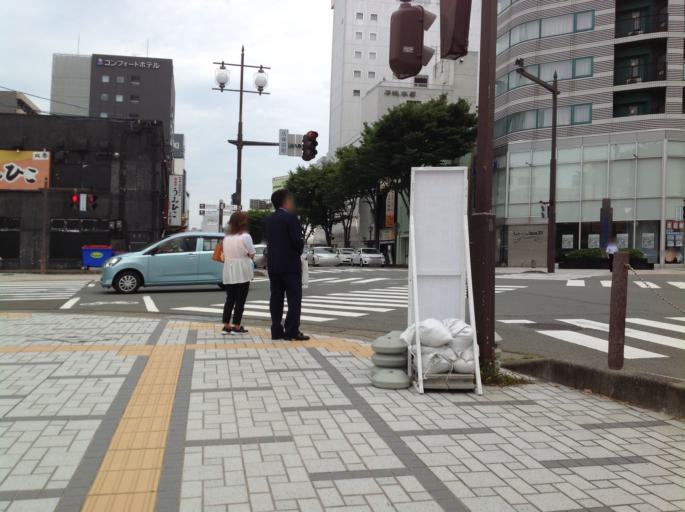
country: JP
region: Akita
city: Akita
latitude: 39.7179
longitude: 140.1250
